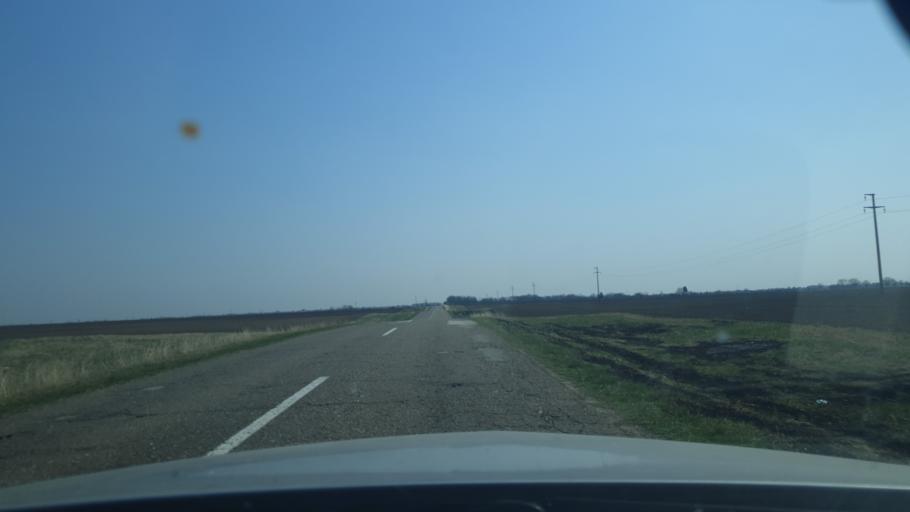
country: RS
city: Sasinci
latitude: 45.0275
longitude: 19.7570
